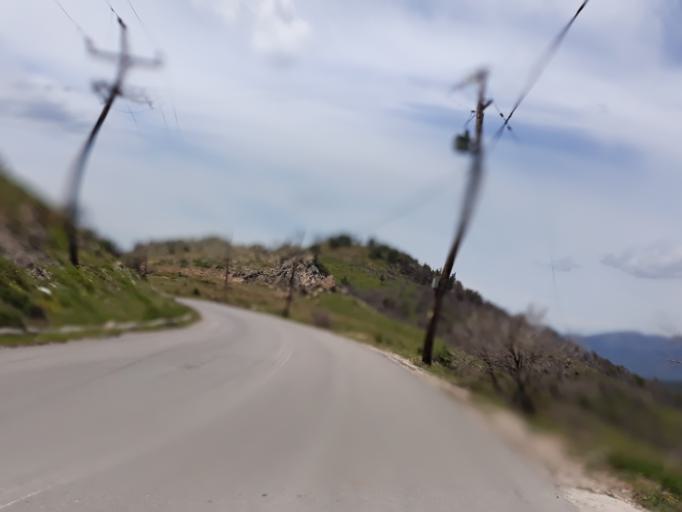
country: GR
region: Attica
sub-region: Nomarchia Dytikis Attikis
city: Magoula
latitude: 38.1640
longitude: 23.5406
